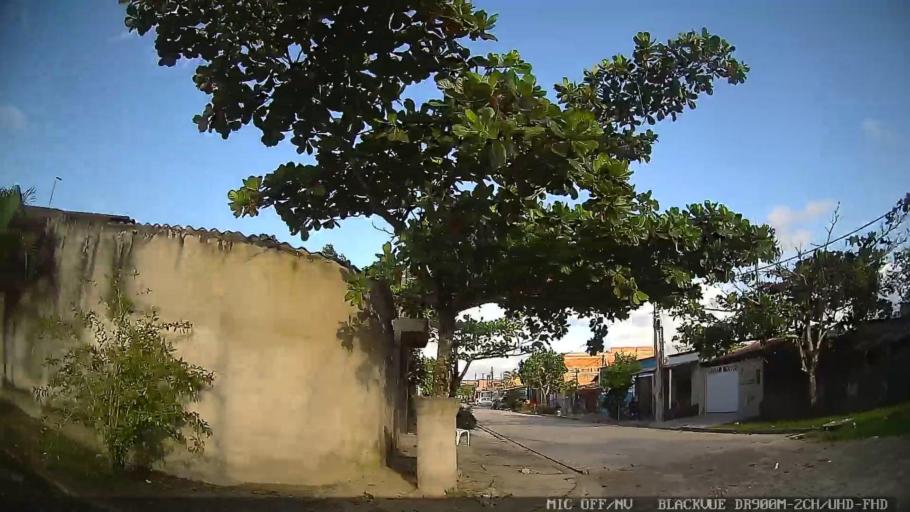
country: BR
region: Sao Paulo
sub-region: Itanhaem
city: Itanhaem
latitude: -24.1803
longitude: -46.8301
